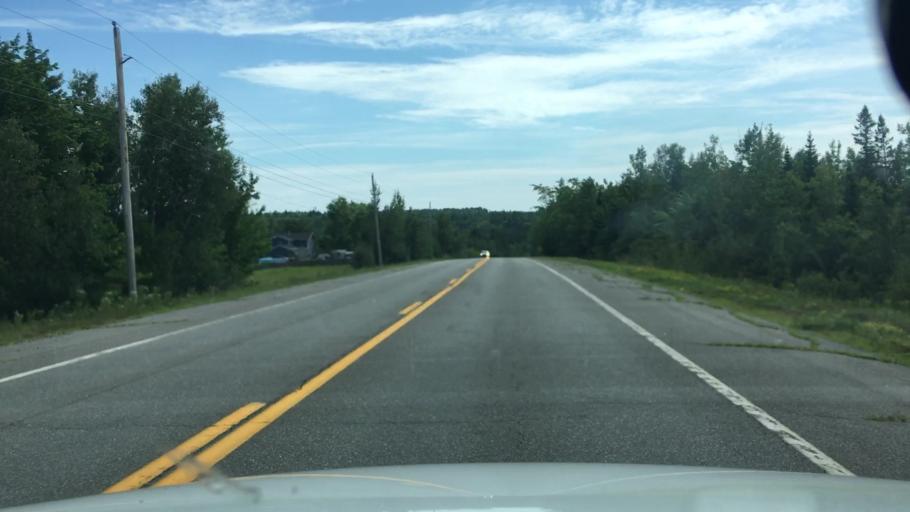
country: CA
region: New Brunswick
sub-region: Charlotte County
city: Saint Andrews
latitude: 45.0396
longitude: -67.1129
